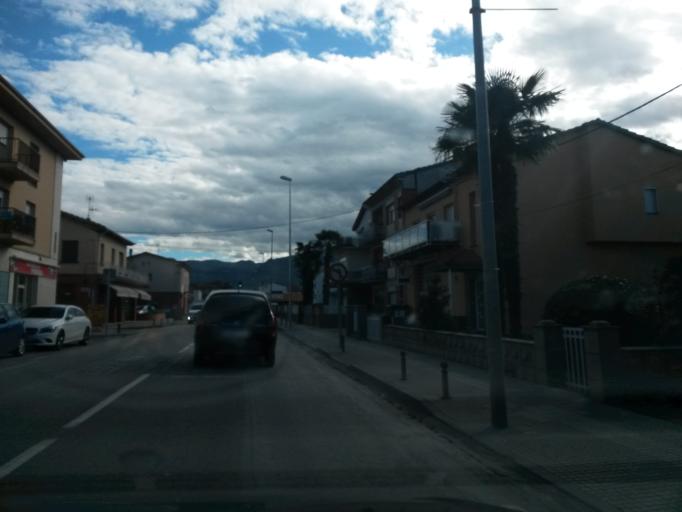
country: ES
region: Catalonia
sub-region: Provincia de Girona
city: Bas
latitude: 42.1453
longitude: 2.4591
